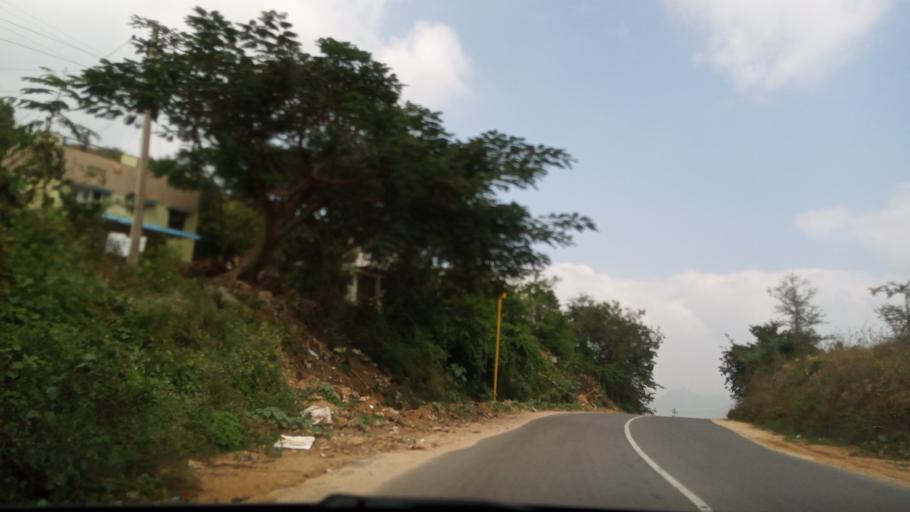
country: IN
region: Andhra Pradesh
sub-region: Chittoor
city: Madanapalle
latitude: 13.5853
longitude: 78.5231
